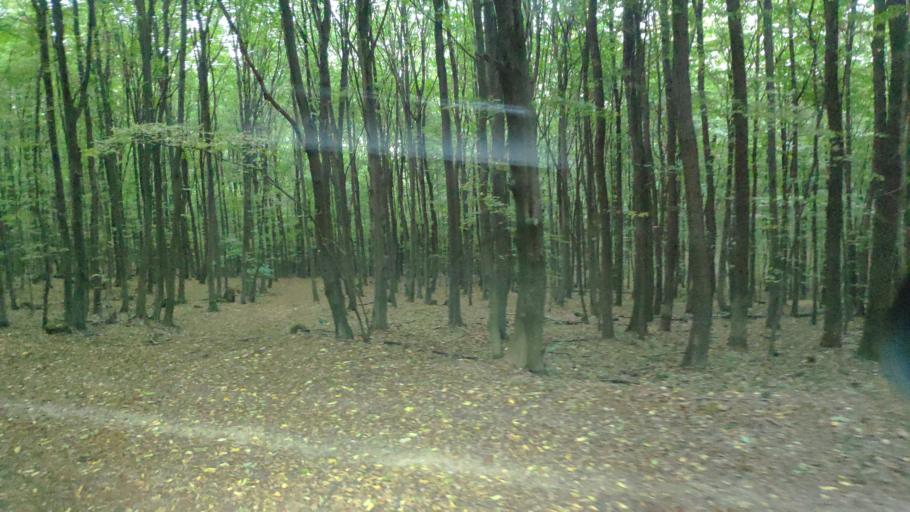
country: SK
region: Kosicky
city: Kosice
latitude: 48.6981
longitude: 21.1983
